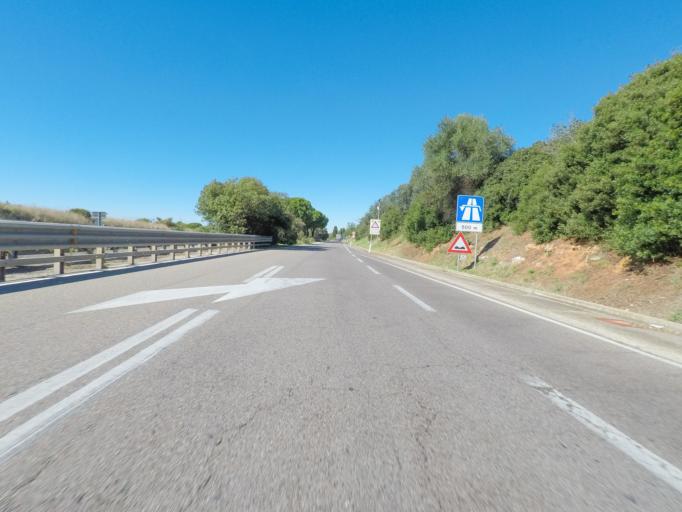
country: IT
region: Tuscany
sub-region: Provincia di Grosseto
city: Orbetello Scalo
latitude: 42.4474
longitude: 11.2577
